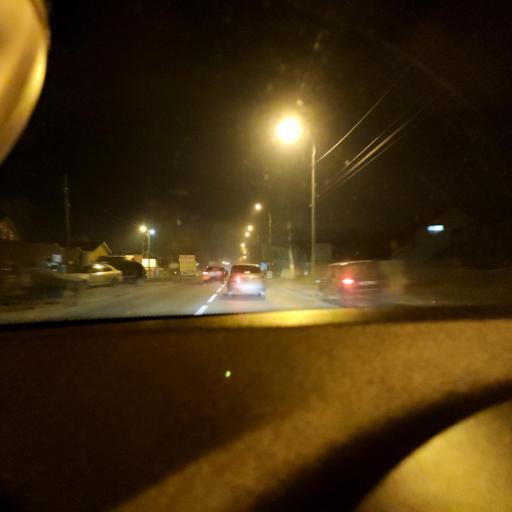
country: RU
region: Samara
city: Smyshlyayevka
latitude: 53.2457
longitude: 50.3459
